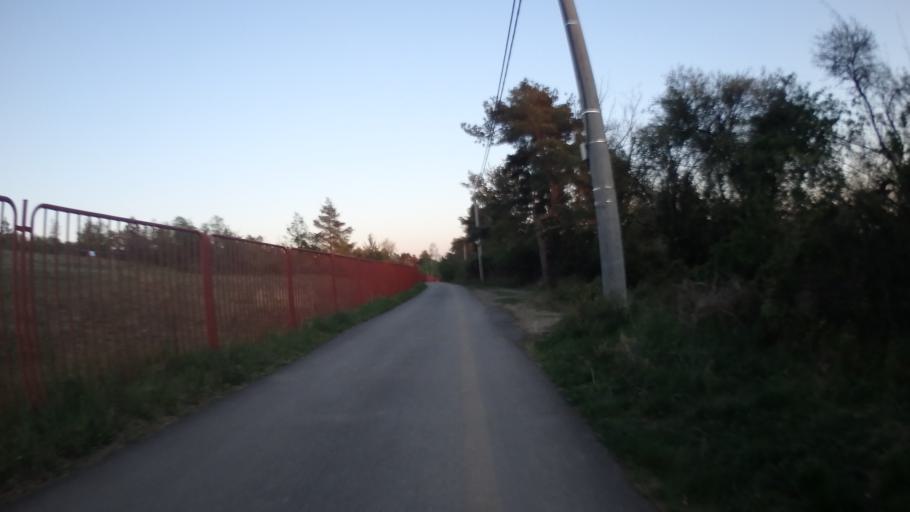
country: CZ
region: South Moravian
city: Ostopovice
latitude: 49.1834
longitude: 16.5501
